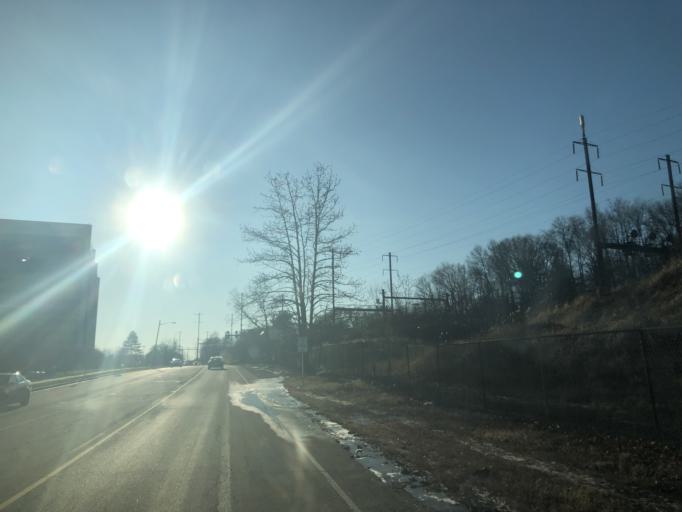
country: US
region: New Jersey
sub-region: Middlesex County
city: Iselin
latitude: 40.5647
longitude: -74.3325
